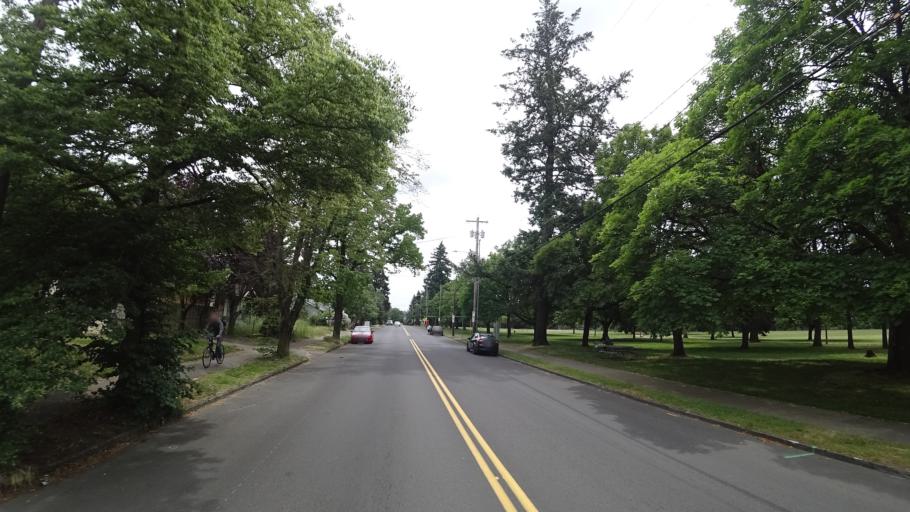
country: US
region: Oregon
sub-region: Multnomah County
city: Lents
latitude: 45.4872
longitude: -122.5686
